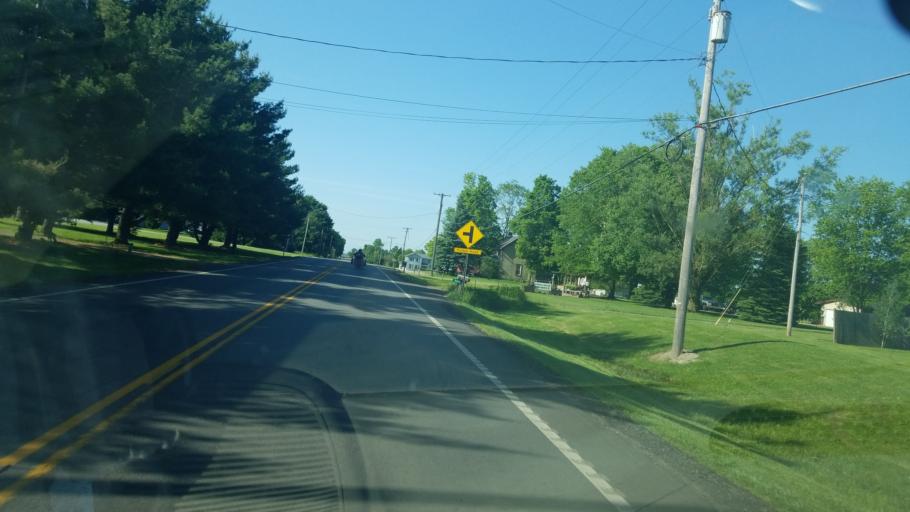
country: US
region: Ohio
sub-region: Wayne County
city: Smithville
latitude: 40.9020
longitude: -81.9141
